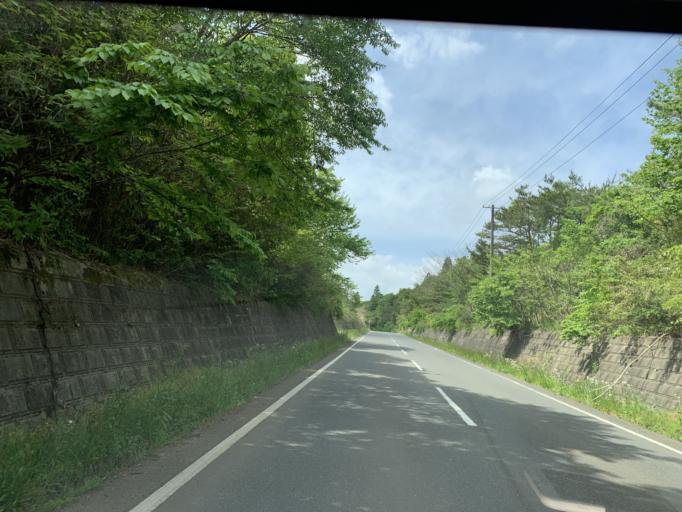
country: JP
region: Iwate
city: Ichinoseki
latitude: 38.8075
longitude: 141.0117
